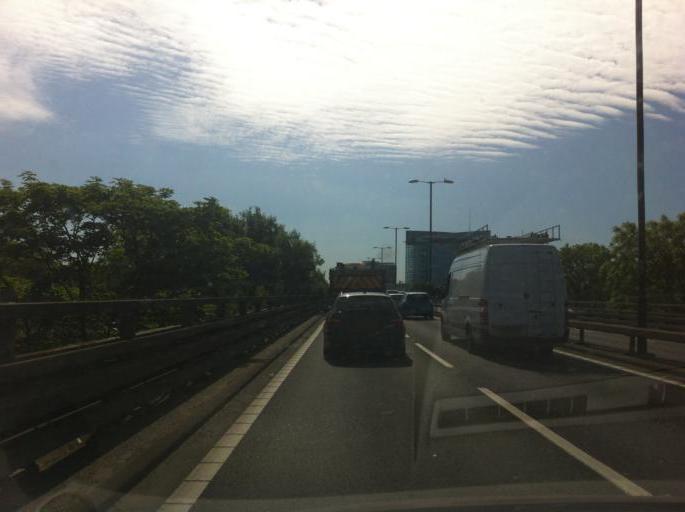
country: GB
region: England
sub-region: Greater London
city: Brentford
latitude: 51.4916
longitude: -0.3221
